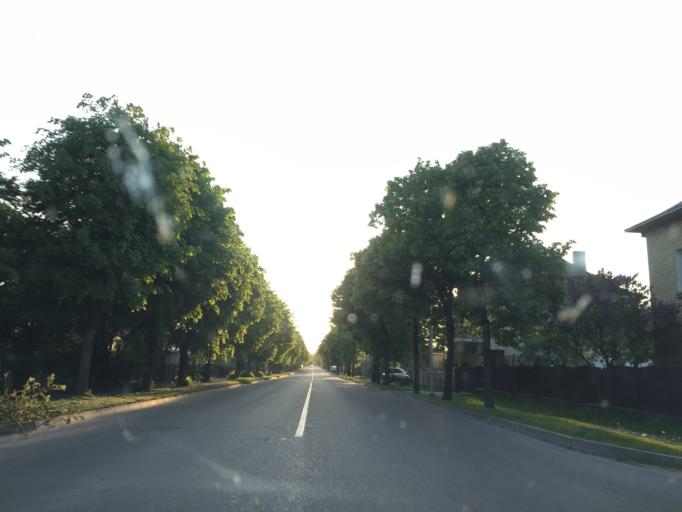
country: LT
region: Siauliu apskritis
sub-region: Siauliai
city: Siauliai
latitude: 55.9536
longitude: 23.3349
